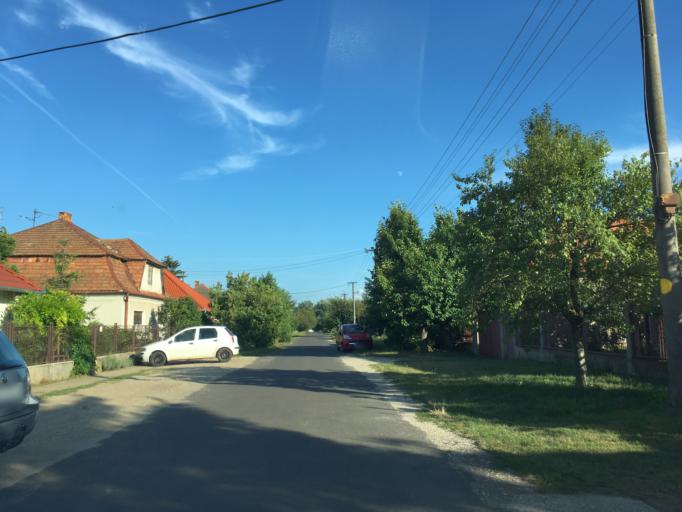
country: SK
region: Nitriansky
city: Svodin
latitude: 47.9000
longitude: 18.4121
